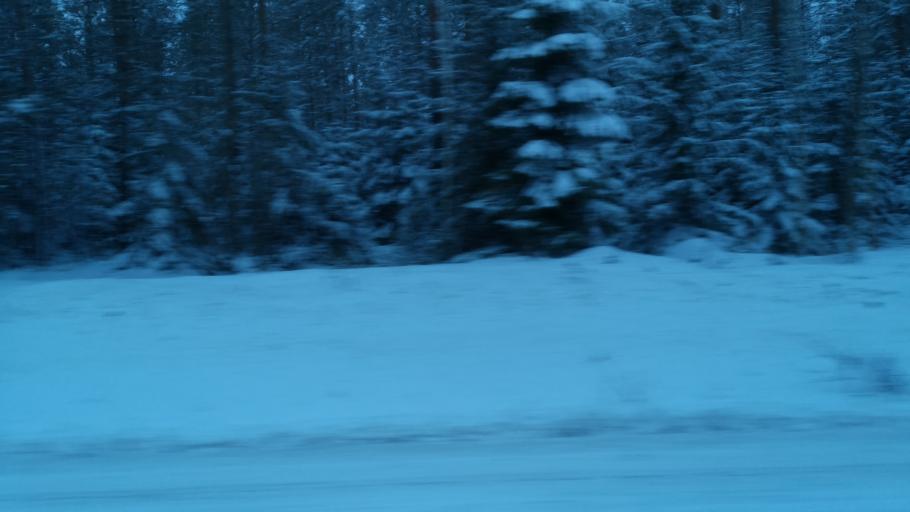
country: FI
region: Southern Savonia
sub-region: Savonlinna
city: Savonlinna
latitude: 61.9902
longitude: 28.7781
